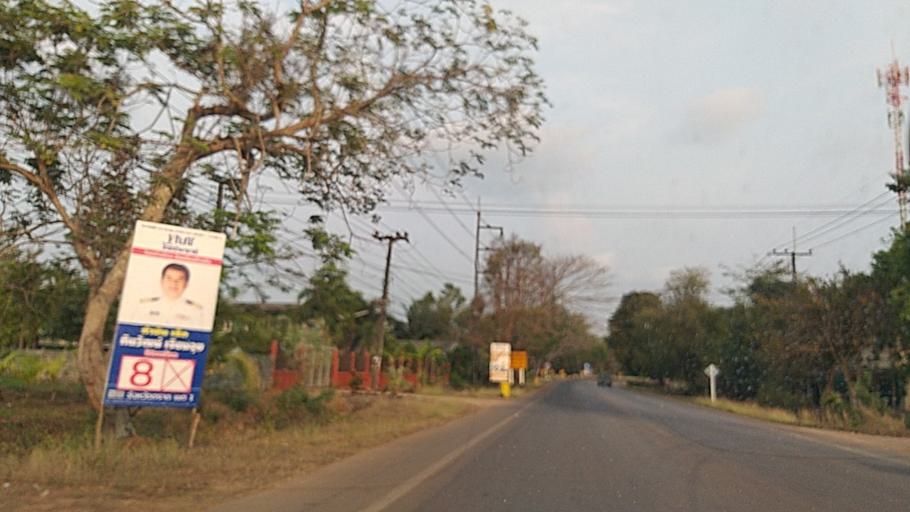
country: TH
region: Trat
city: Laem Ngop
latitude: 12.2326
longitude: 102.3030
